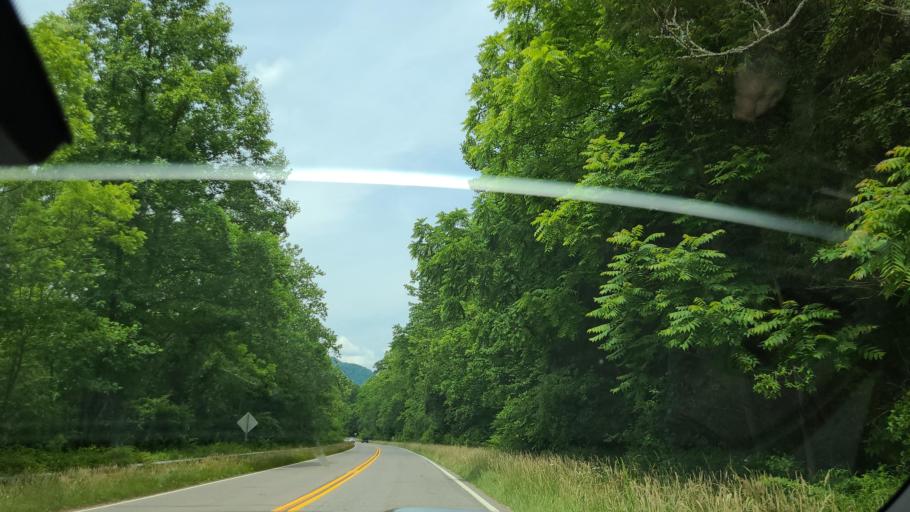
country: US
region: North Carolina
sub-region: Macon County
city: Franklin
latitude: 35.1426
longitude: -83.2903
